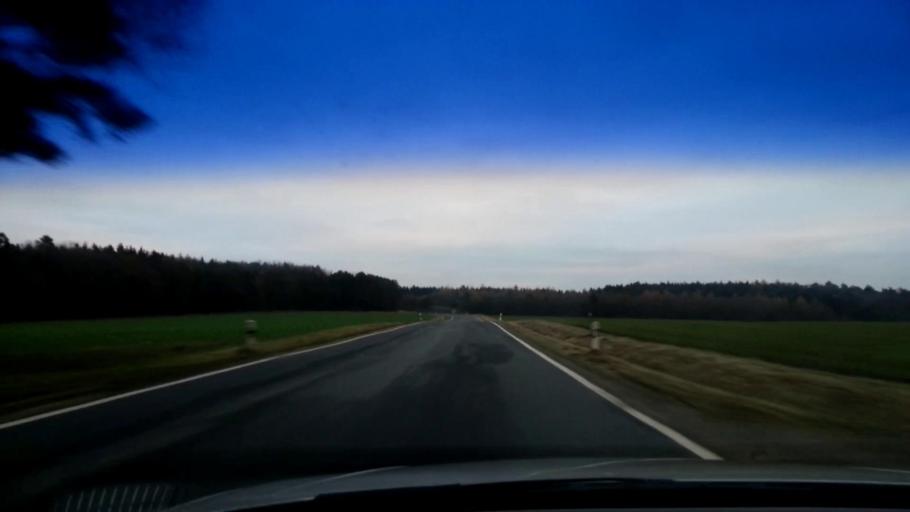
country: DE
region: Bavaria
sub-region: Regierungsbezirk Mittelfranken
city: Muhlhausen
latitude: 49.7986
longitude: 10.7840
